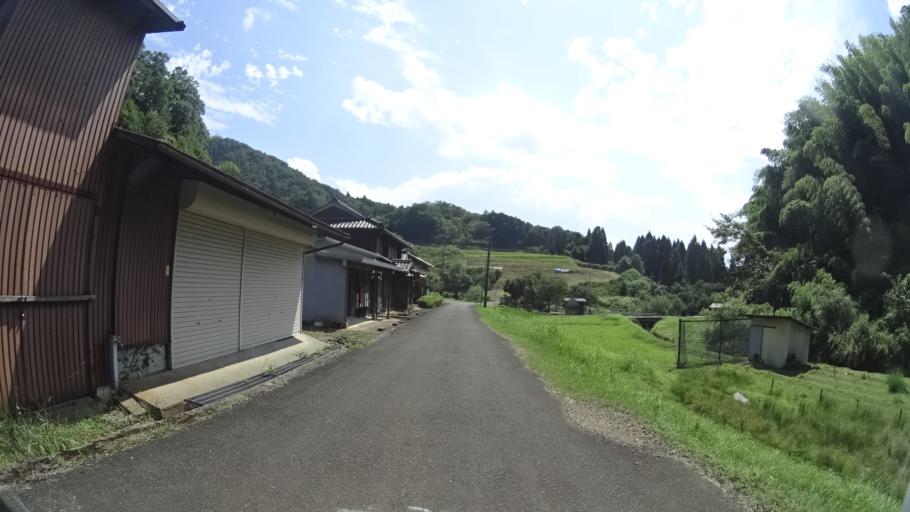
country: JP
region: Kyoto
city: Maizuru
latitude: 35.3857
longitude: 135.3589
